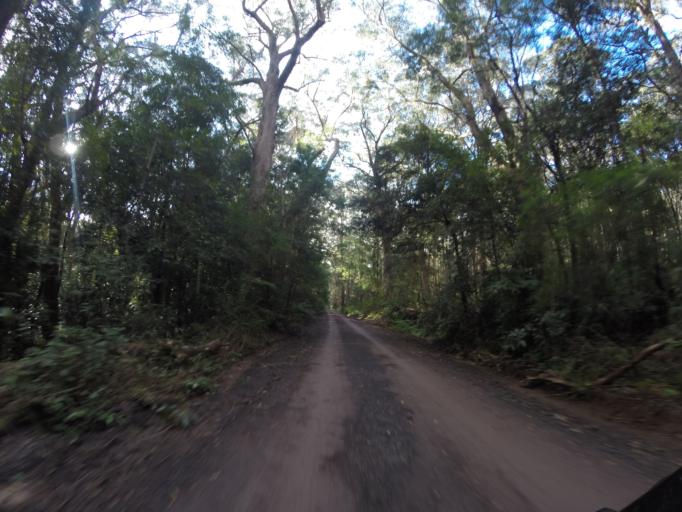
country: AU
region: New South Wales
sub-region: Wollongong
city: Cordeaux Heights
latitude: -34.4152
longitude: 150.7840
